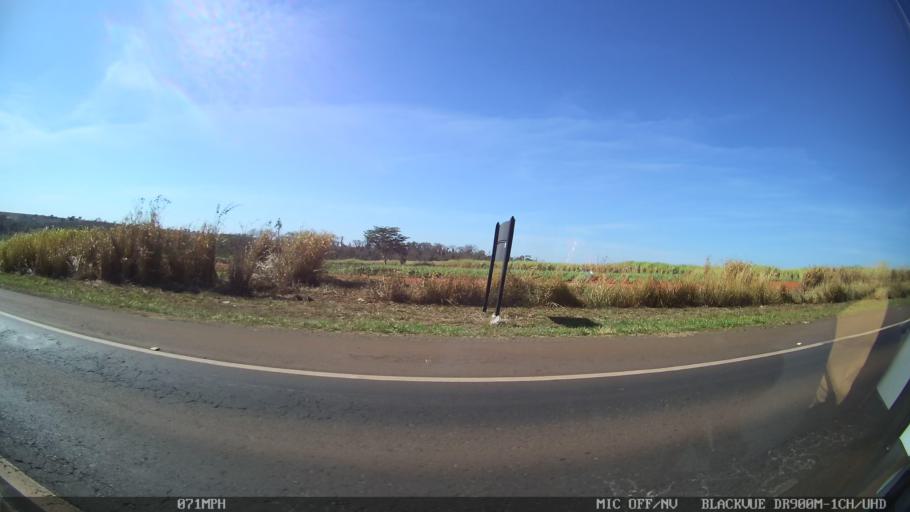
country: BR
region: Sao Paulo
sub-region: Olimpia
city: Olimpia
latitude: -20.7096
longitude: -48.8808
